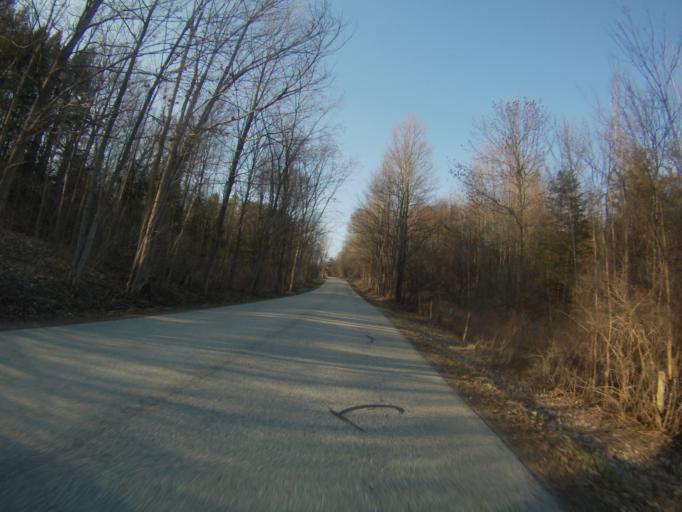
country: US
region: Vermont
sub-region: Addison County
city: Middlebury (village)
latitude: 44.0320
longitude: -73.1452
